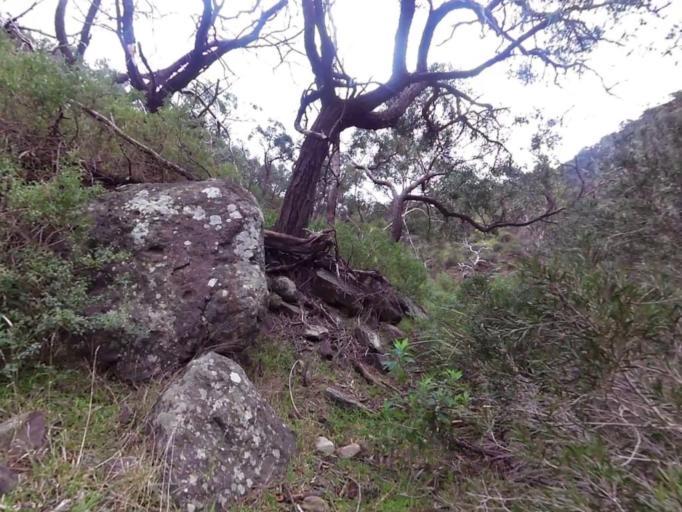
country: AU
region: Victoria
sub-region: Moorabool
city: Bacchus Marsh
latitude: -37.6620
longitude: 144.3518
